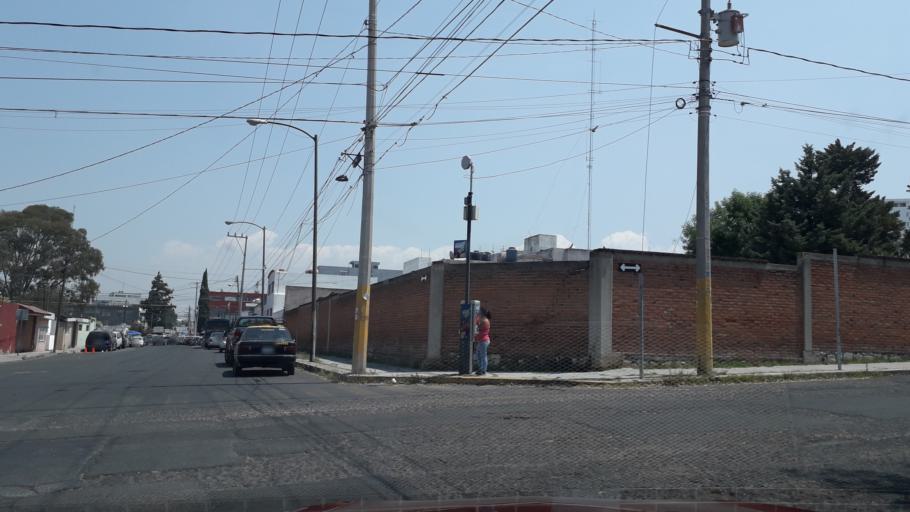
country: MX
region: Puebla
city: Puebla
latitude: 19.0549
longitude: -98.2346
